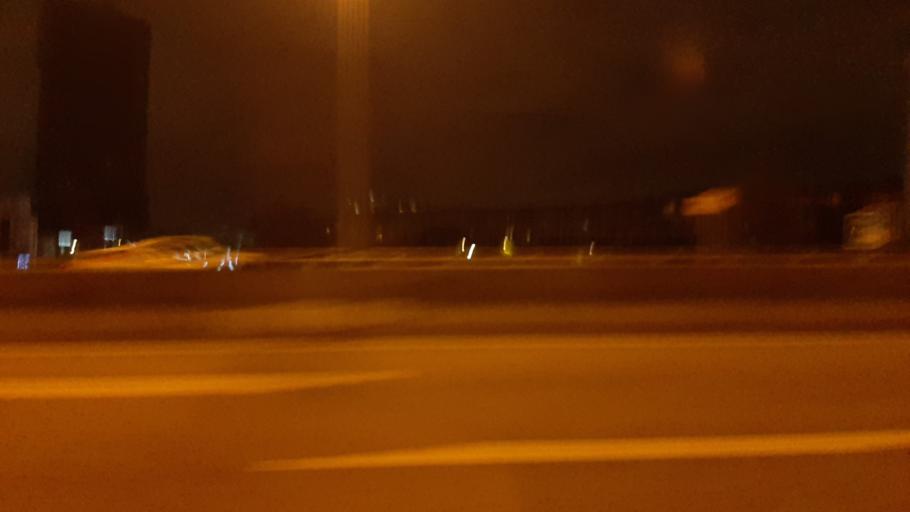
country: MY
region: Kuala Lumpur
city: Kuala Lumpur
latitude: 3.1653
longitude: 101.6480
